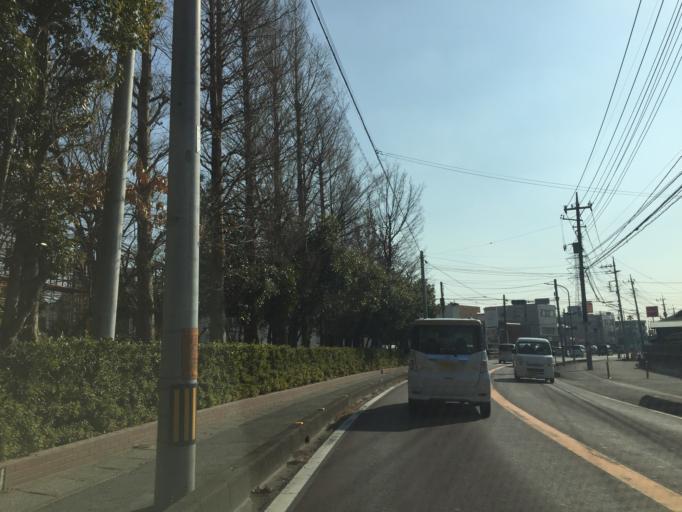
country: JP
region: Saitama
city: Shiki
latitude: 35.8390
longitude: 139.5904
